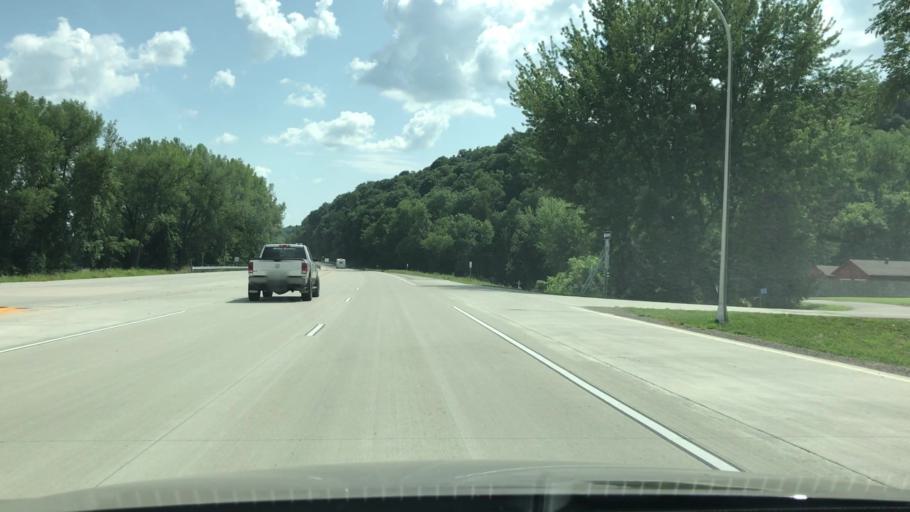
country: US
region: Minnesota
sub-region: Nicollet County
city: North Mankato
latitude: 44.2624
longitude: -94.0265
